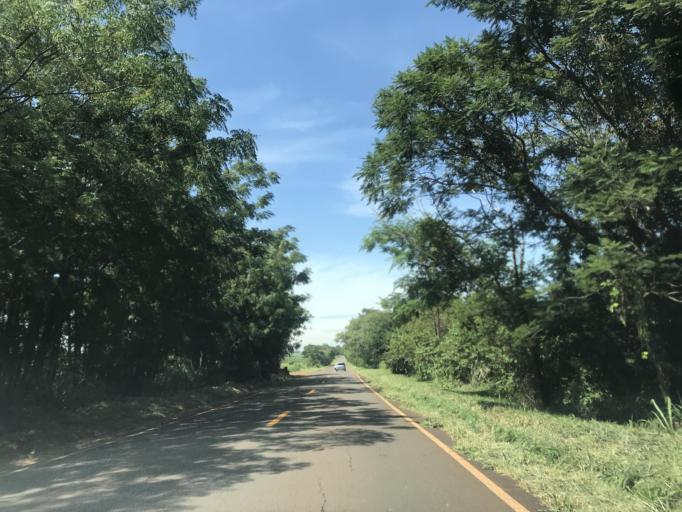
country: BR
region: Parana
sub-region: Paranavai
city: Nova Aurora
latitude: -22.8129
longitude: -52.6545
